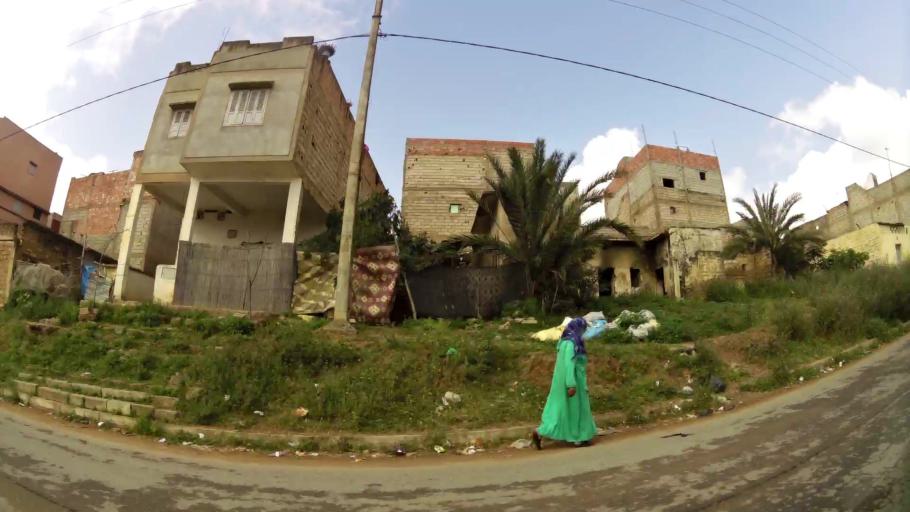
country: MA
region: Rabat-Sale-Zemmour-Zaer
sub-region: Khemisset
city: Tiflet
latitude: 33.8970
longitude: -6.3137
